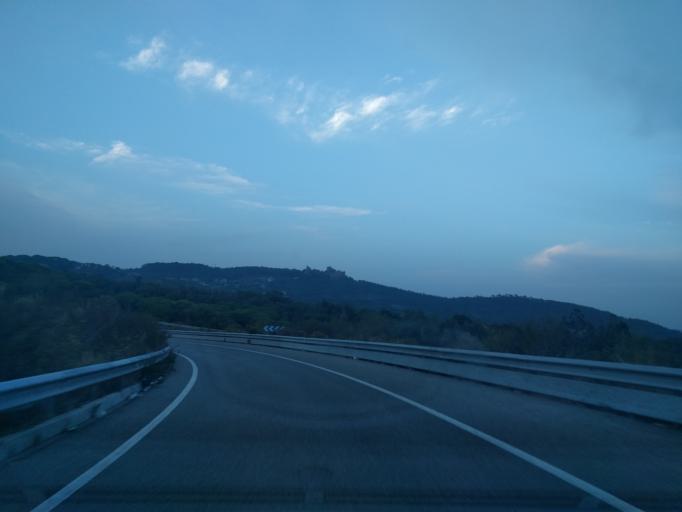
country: ES
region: Catalonia
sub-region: Provincia de Barcelona
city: Palafolls
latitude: 41.6710
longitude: 2.7272
